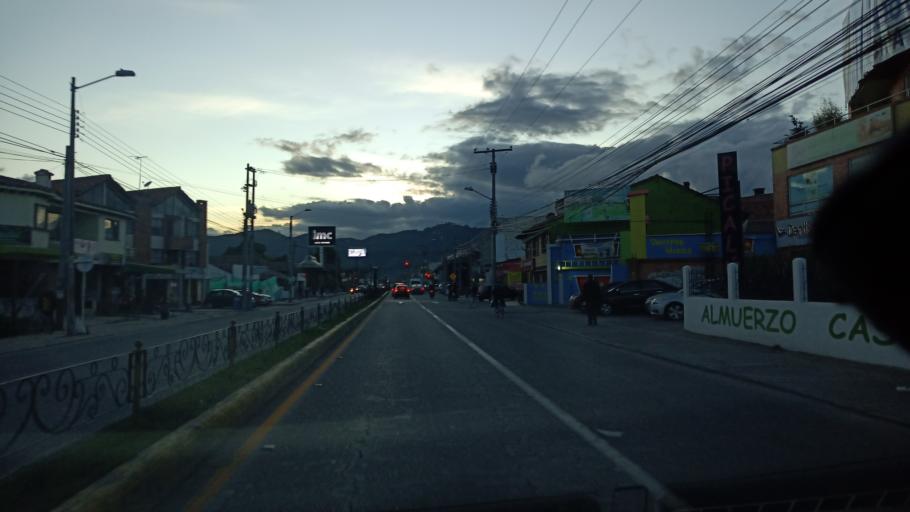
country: CO
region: Cundinamarca
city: Chia
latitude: 4.8636
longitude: -74.0494
